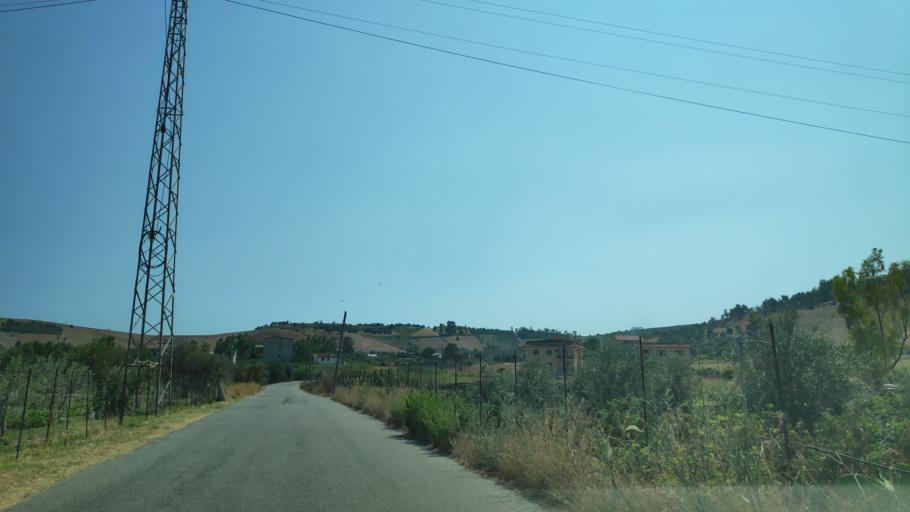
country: IT
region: Calabria
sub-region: Provincia di Reggio Calabria
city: Monasterace Marina
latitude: 38.4259
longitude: 16.5437
